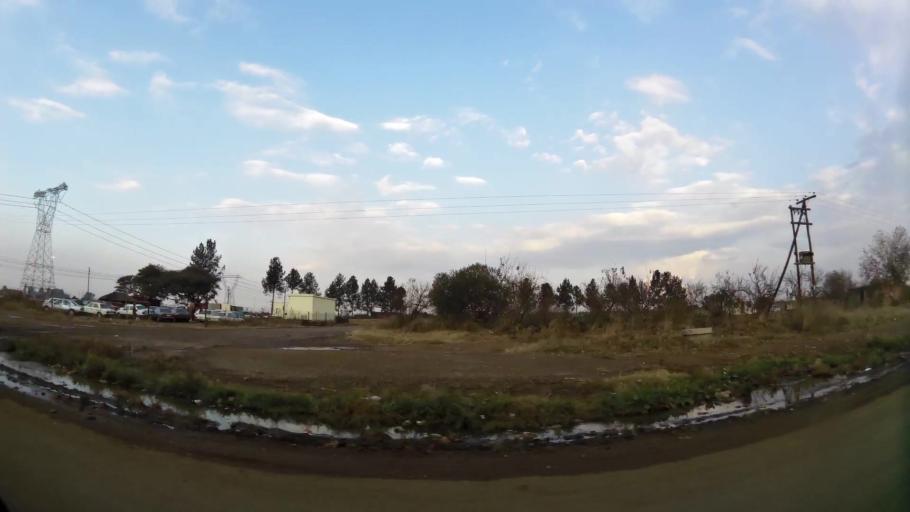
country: ZA
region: Gauteng
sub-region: City of Johannesburg Metropolitan Municipality
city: Orange Farm
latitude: -26.5540
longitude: 27.8306
